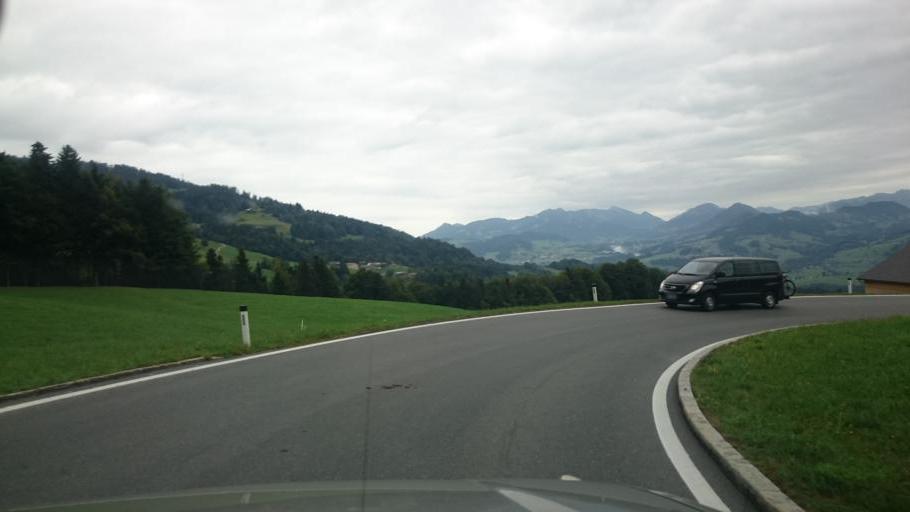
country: AT
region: Vorarlberg
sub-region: Politischer Bezirk Bregenz
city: Andelsbuch
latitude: 47.4184
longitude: 9.8399
